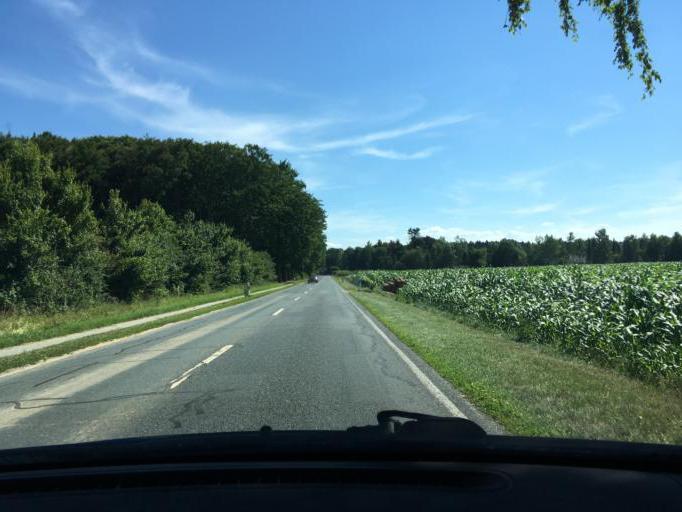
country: DE
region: Lower Saxony
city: Bendestorf
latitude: 53.3550
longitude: 9.9411
